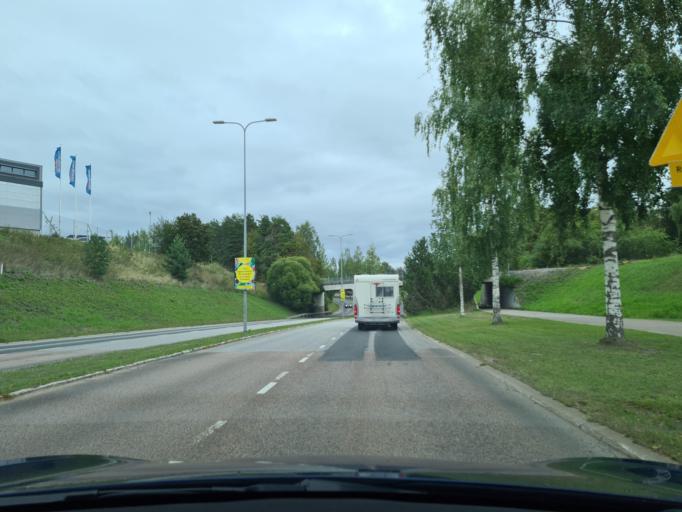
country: FI
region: South Karelia
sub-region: Lappeenranta
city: Lappeenranta
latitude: 61.0492
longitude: 28.1830
